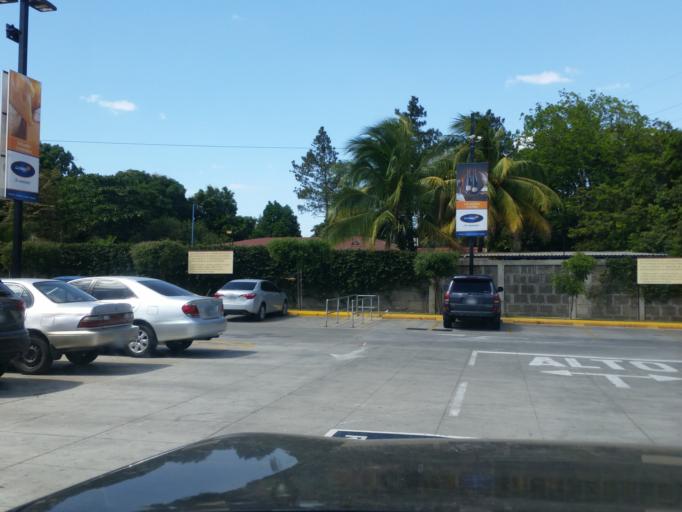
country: NI
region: Masaya
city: Ticuantepe
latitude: 12.0716
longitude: -86.2182
